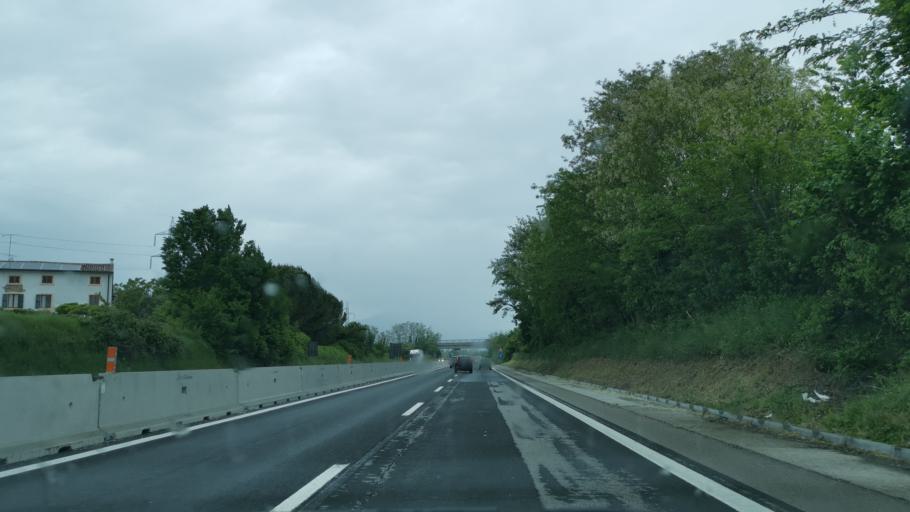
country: IT
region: Veneto
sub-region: Provincia di Verona
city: Castelnuovo del Garda
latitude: 45.4447
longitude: 10.7461
